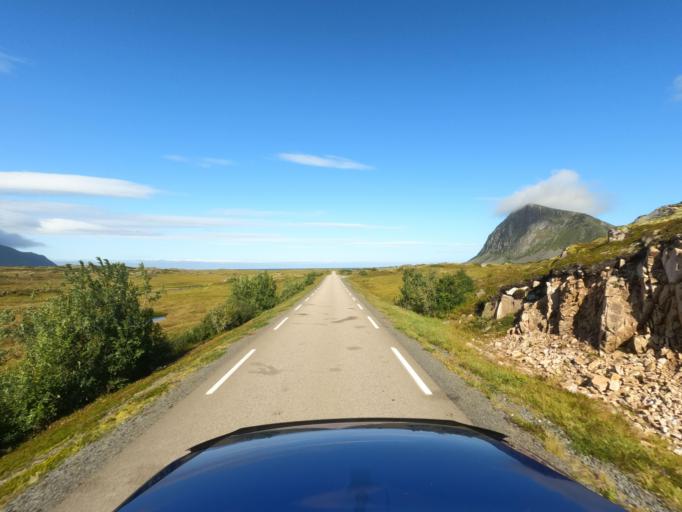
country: NO
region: Nordland
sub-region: Vestvagoy
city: Evjen
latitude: 68.3117
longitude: 14.0950
